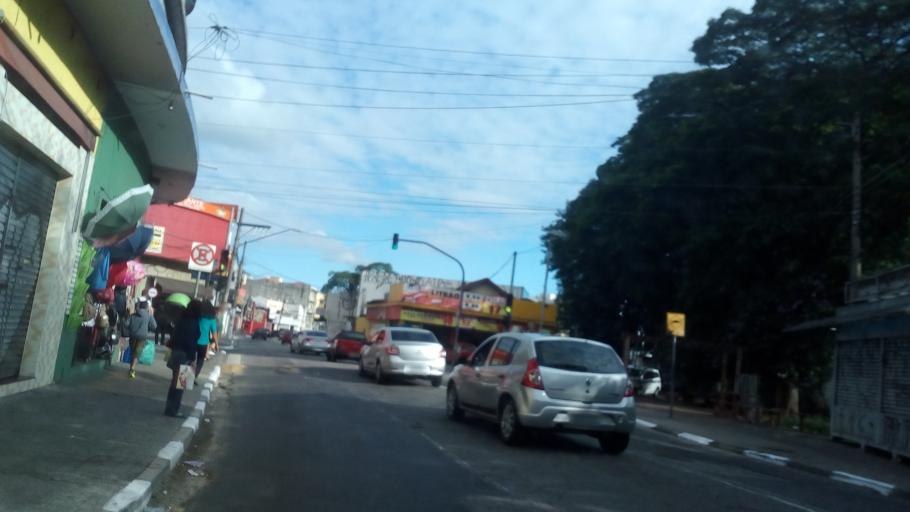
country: BR
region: Sao Paulo
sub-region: Guarulhos
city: Guarulhos
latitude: -23.4612
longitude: -46.5346
